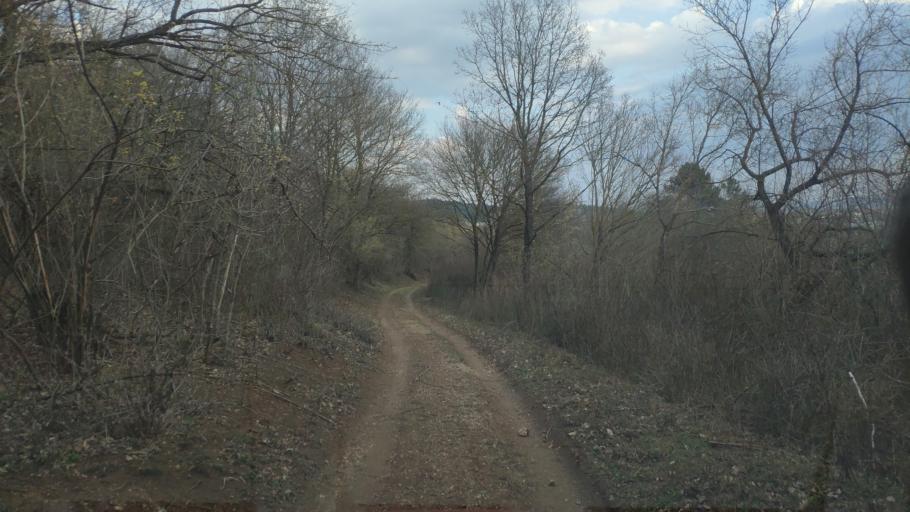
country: SK
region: Kosicky
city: Moldava nad Bodvou
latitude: 48.6200
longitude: 20.9277
